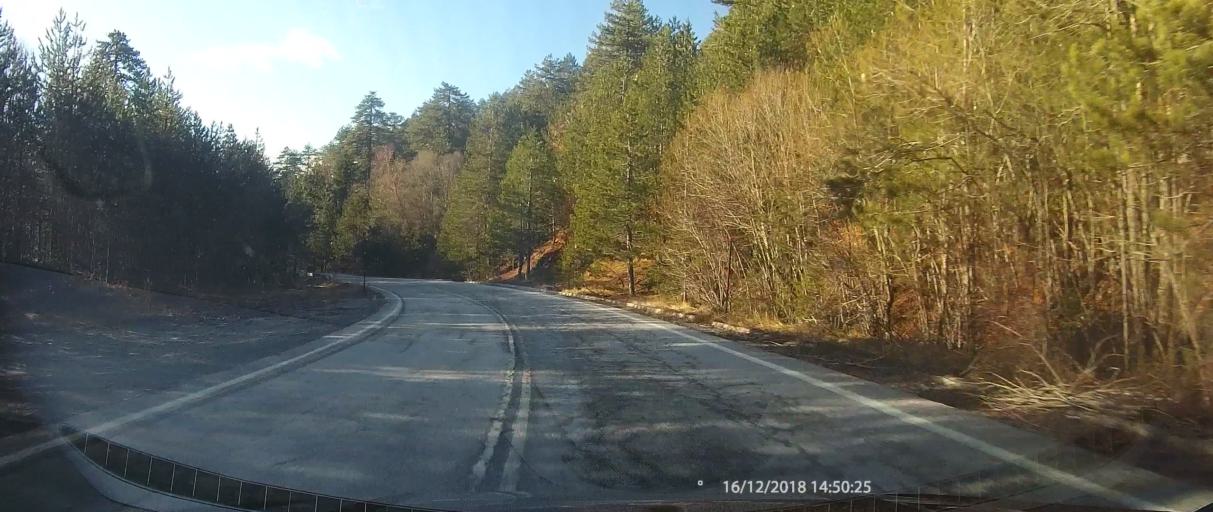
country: GR
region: West Macedonia
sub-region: Nomos Kastorias
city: Nestorio
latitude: 40.2081
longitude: 21.0803
